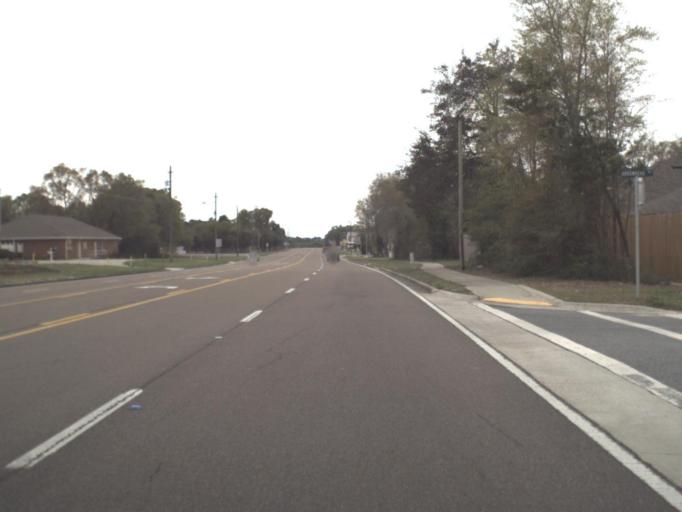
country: US
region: Florida
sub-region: Okaloosa County
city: Niceville
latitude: 30.5306
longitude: -86.4936
